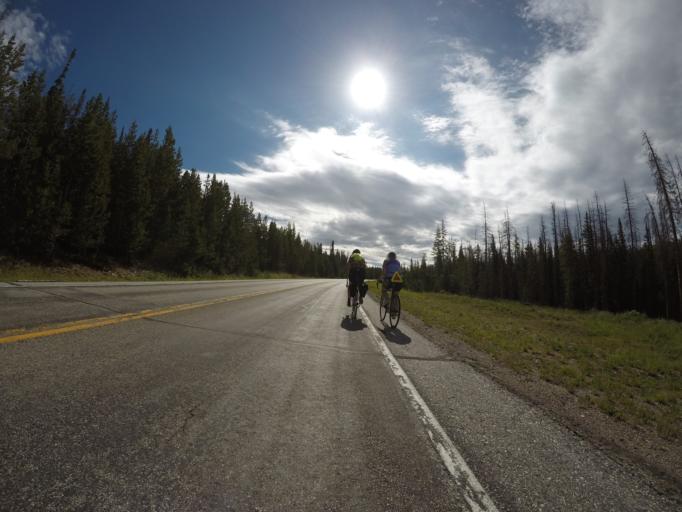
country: US
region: Wyoming
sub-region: Carbon County
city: Saratoga
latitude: 41.3267
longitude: -106.4396
